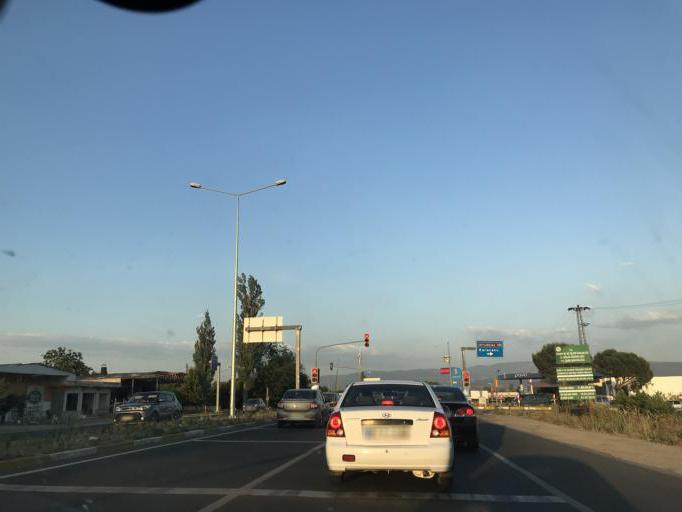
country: TR
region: Aydin
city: Kuyucak
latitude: 37.9056
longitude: 28.4928
